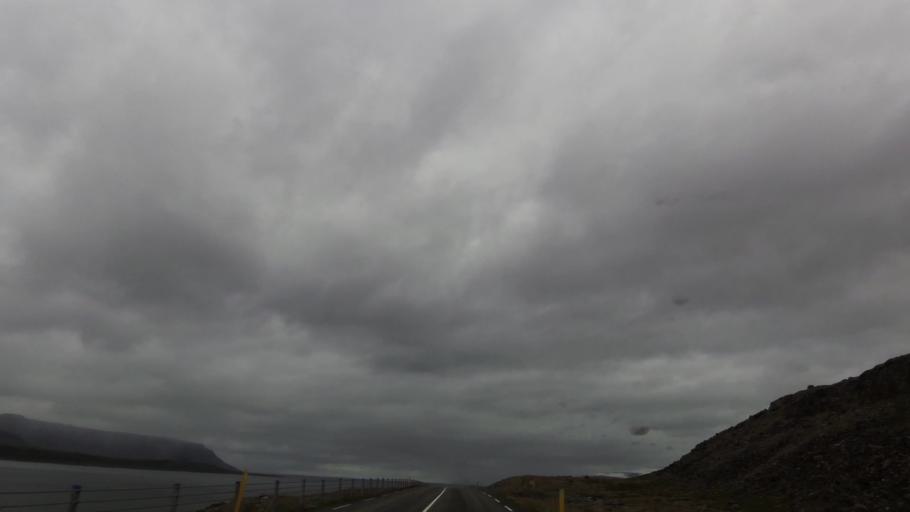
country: IS
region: Westfjords
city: Isafjoerdur
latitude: 66.0002
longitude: -22.7827
